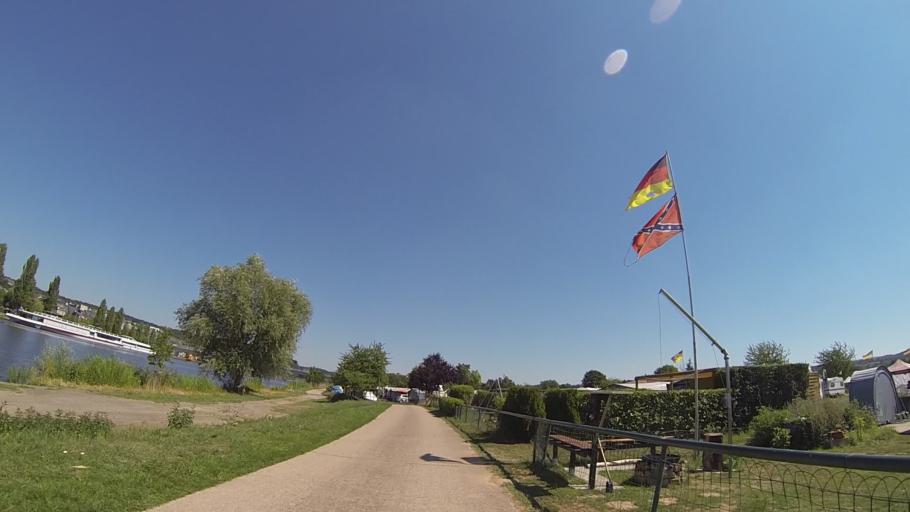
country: LU
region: Grevenmacher
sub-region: Canton de Remich
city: Remich
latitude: 49.5402
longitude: 6.3688
